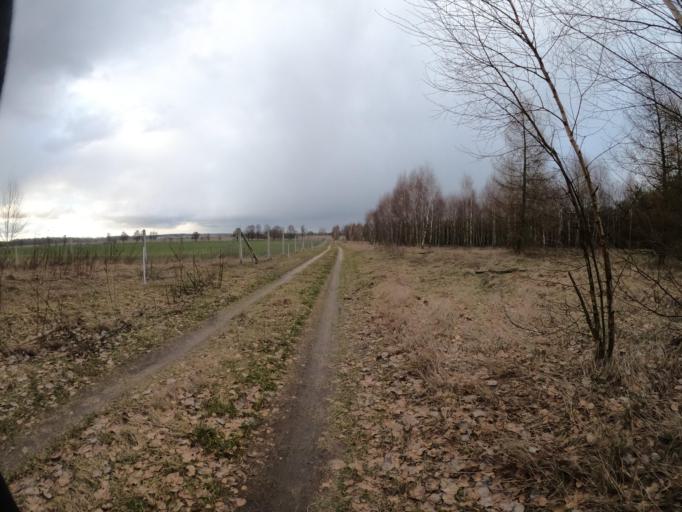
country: PL
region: Greater Poland Voivodeship
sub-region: Powiat zlotowski
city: Sypniewo
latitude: 53.4549
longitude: 16.5919
